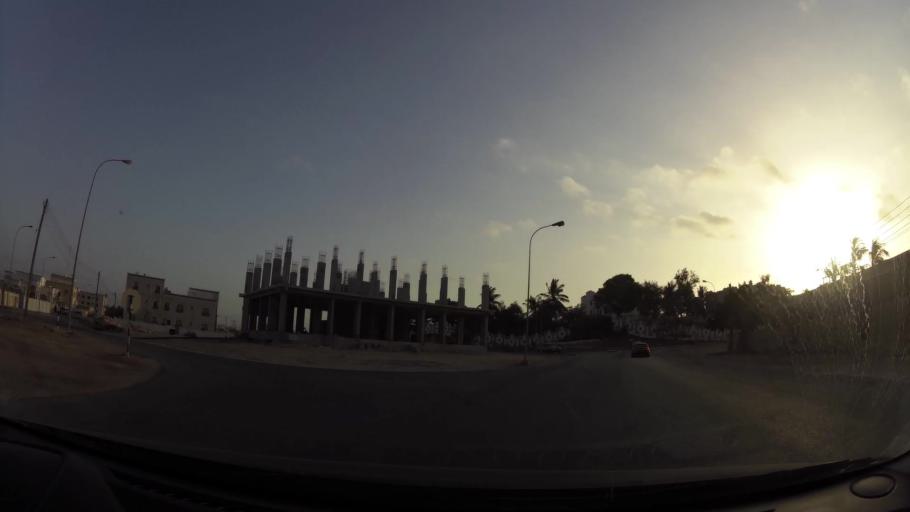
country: OM
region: Zufar
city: Salalah
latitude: 17.0033
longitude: 54.0334
